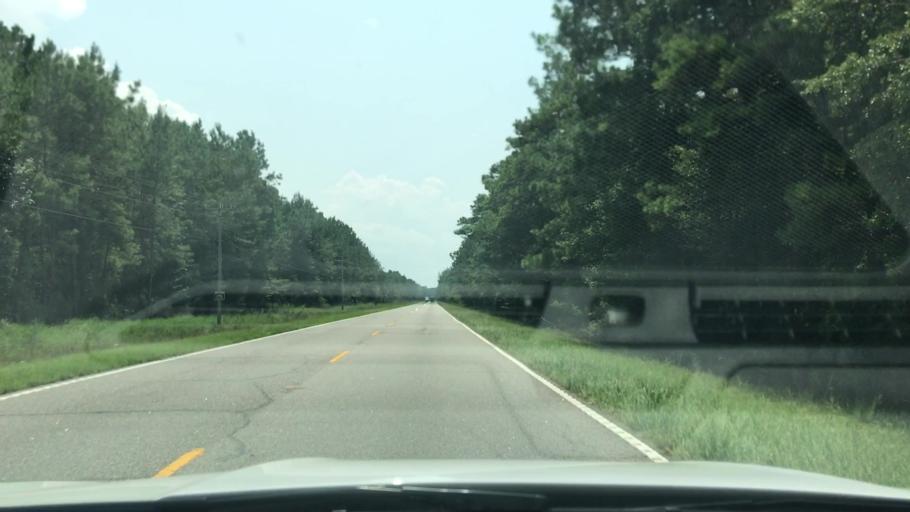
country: US
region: South Carolina
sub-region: Georgetown County
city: Georgetown
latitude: 33.5059
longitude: -79.2550
